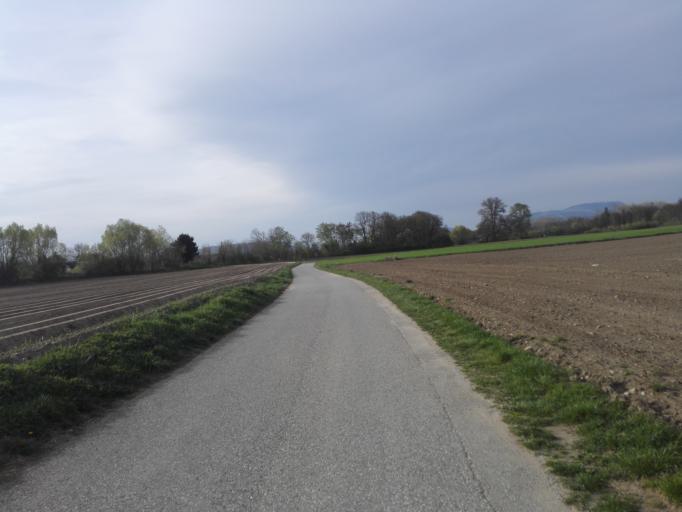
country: AT
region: Styria
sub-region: Politischer Bezirk Graz-Umgebung
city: Feldkirchen bei Graz
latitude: 47.0061
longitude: 15.4537
